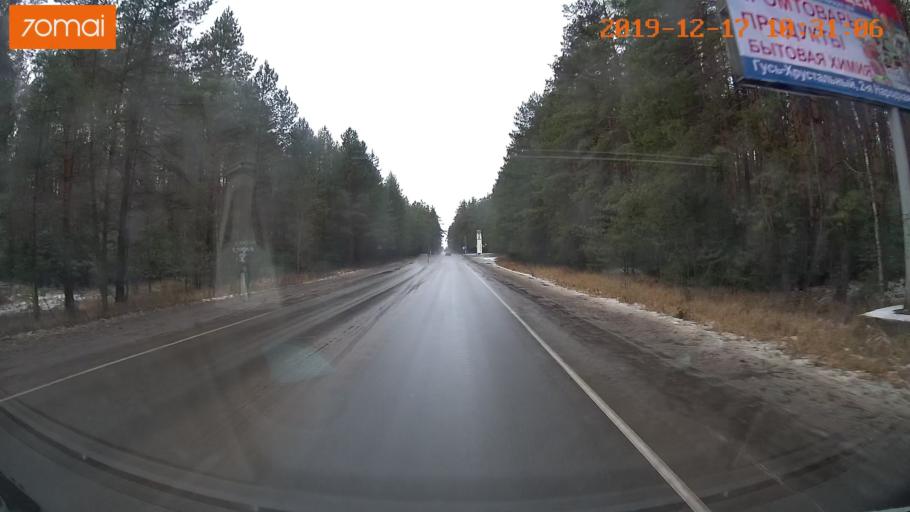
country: RU
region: Vladimir
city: Gus'-Khrustal'nyy
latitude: 55.6378
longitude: 40.7008
